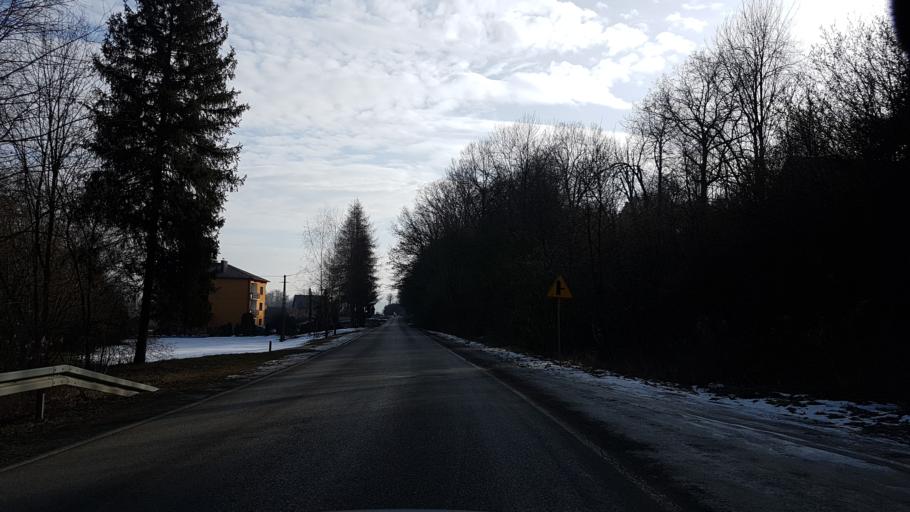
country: PL
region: Lesser Poland Voivodeship
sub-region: Powiat limanowski
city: Lukowica
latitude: 49.6599
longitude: 20.4880
